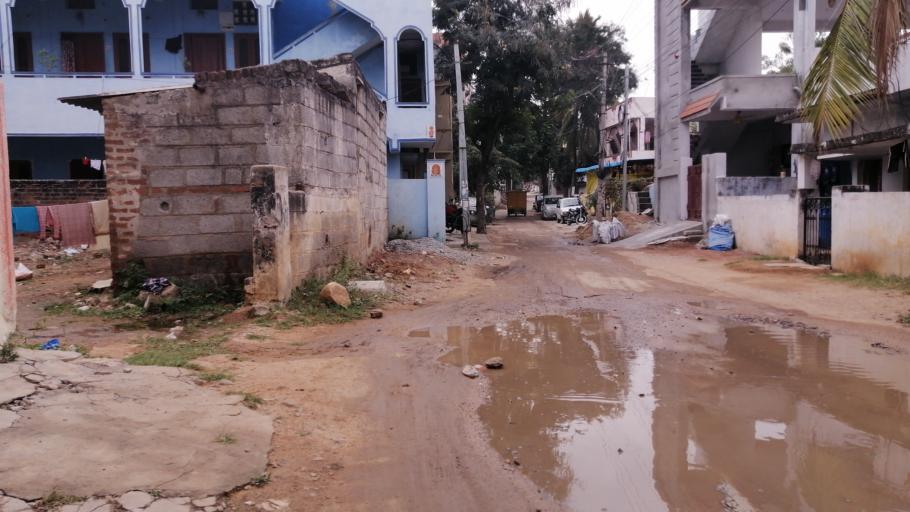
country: IN
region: Telangana
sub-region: Rangareddi
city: Secunderabad
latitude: 17.4824
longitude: 78.5810
